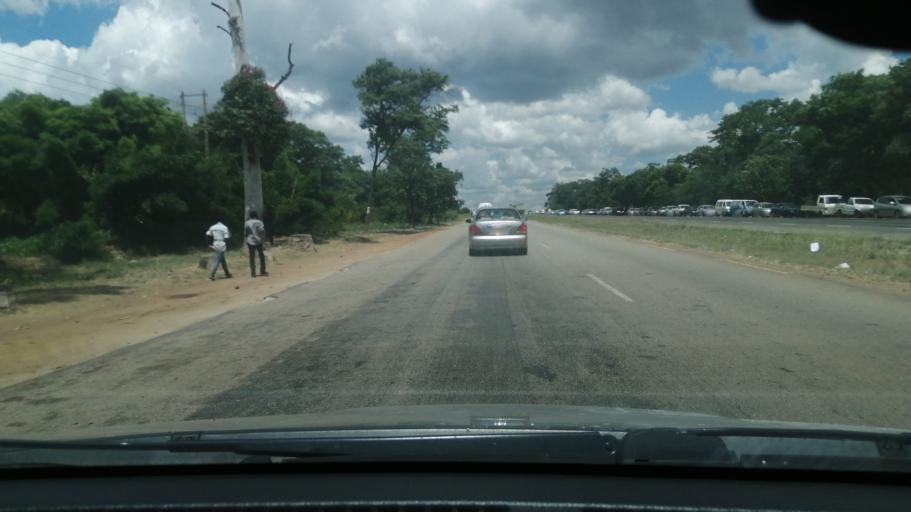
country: ZW
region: Harare
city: Harare
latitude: -17.8207
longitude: 30.8941
